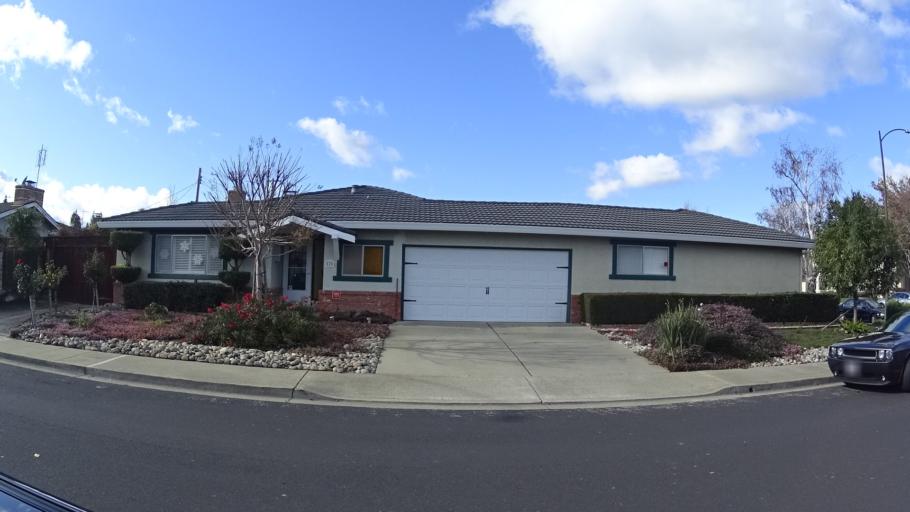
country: US
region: California
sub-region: Santa Clara County
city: Mountain View
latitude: 37.3813
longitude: -122.0588
